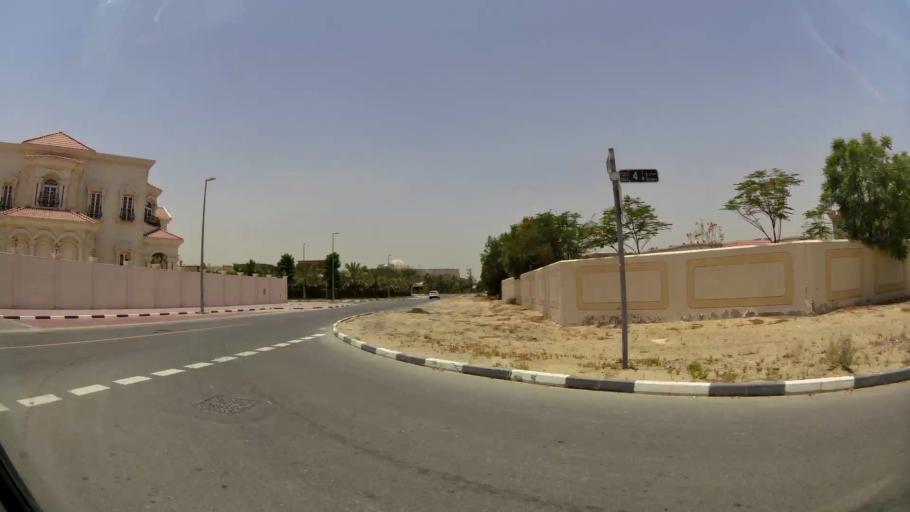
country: AE
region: Ash Shariqah
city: Sharjah
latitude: 25.2357
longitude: 55.4537
